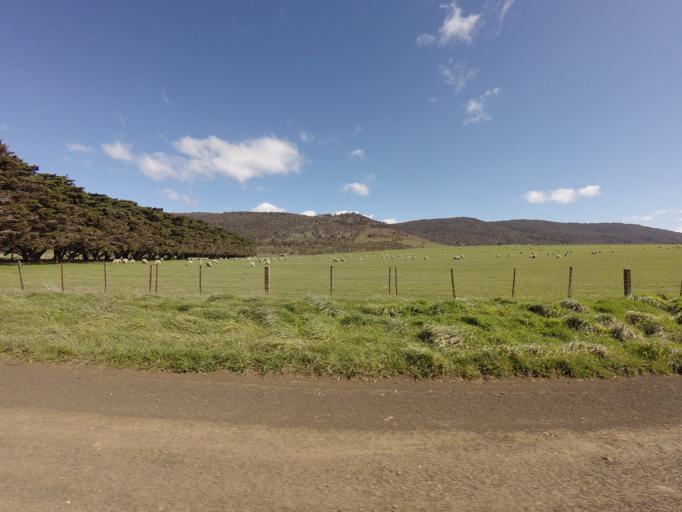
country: AU
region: Tasmania
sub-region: Northern Midlands
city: Evandale
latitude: -41.9541
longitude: 147.4359
